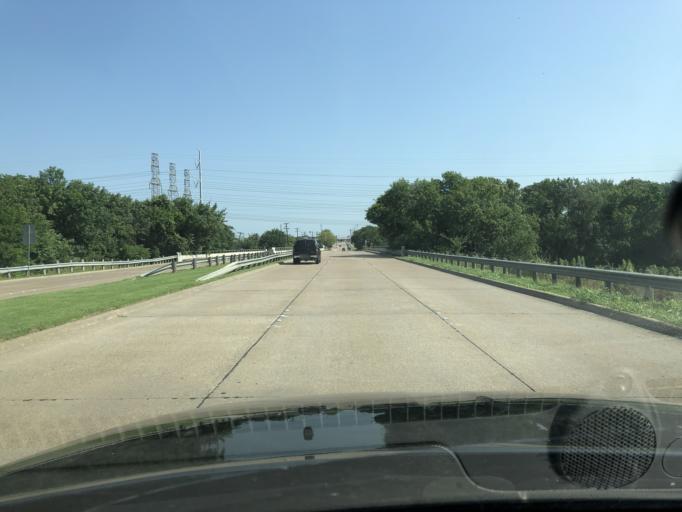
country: US
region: Texas
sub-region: Dallas County
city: Sunnyvale
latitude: 32.8322
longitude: -96.5956
